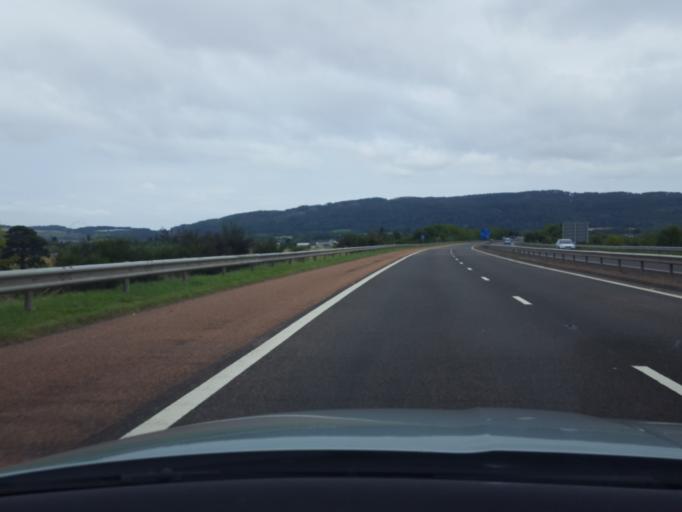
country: GB
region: Scotland
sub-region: Perth and Kinross
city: Bridge of Earn
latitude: 56.3328
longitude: -3.4002
